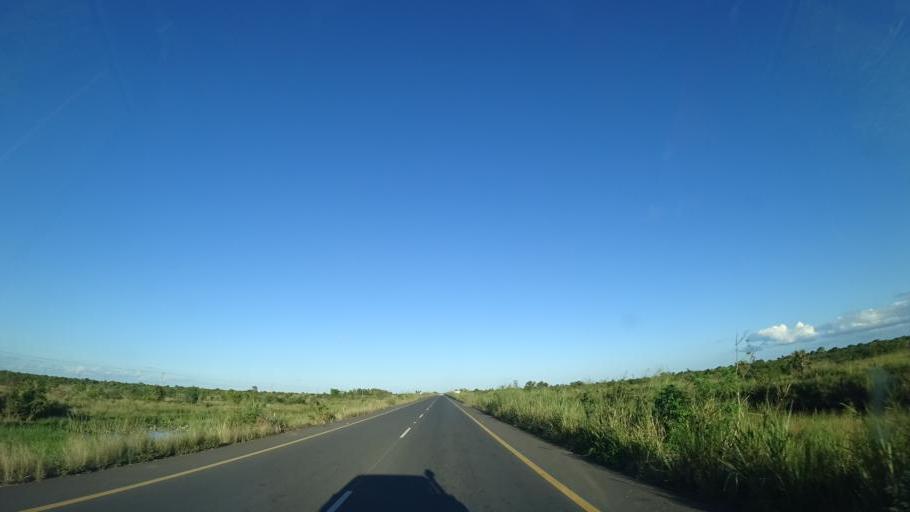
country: MZ
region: Sofala
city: Dondo
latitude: -19.3109
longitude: 34.2731
